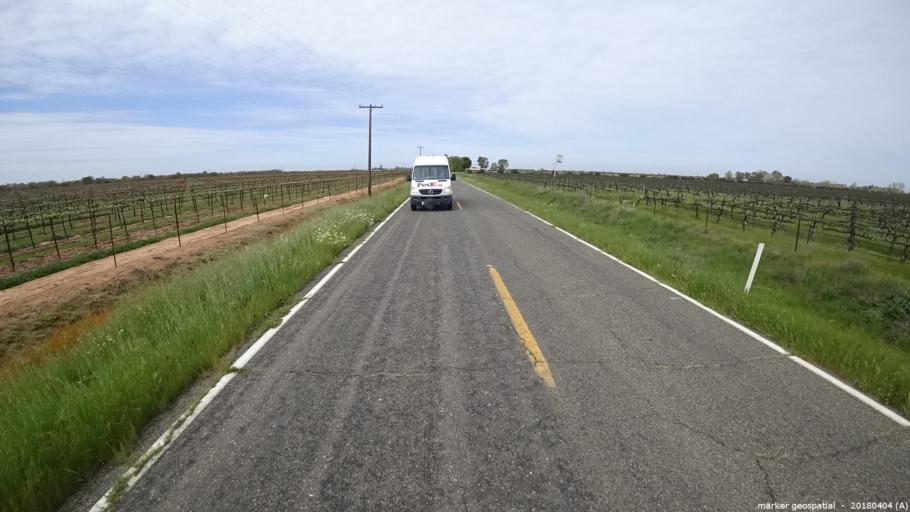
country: US
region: California
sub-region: Sacramento County
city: Clay
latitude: 38.2636
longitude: -121.1736
